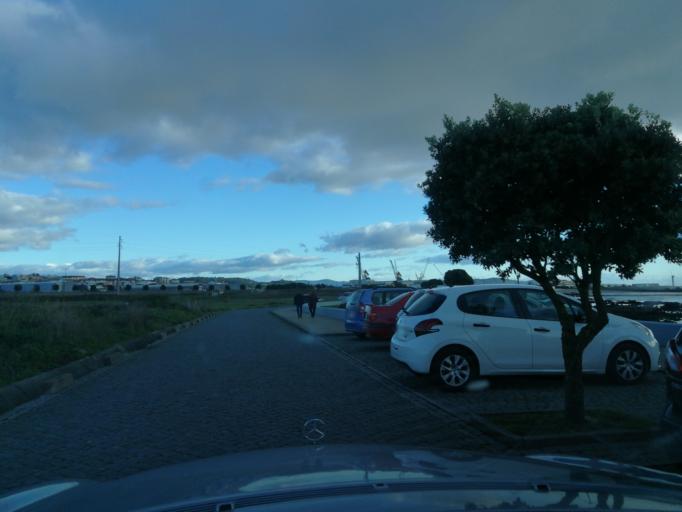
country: PT
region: Viana do Castelo
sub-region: Viana do Castelo
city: Areosa
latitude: 41.6997
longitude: -8.8534
